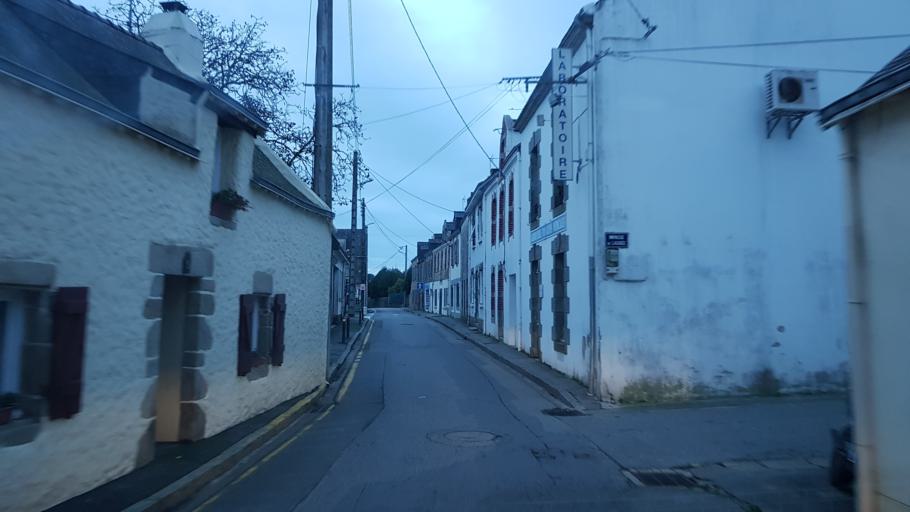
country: FR
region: Brittany
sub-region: Departement du Morbihan
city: Sarzeau
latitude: 47.5283
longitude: -2.7676
